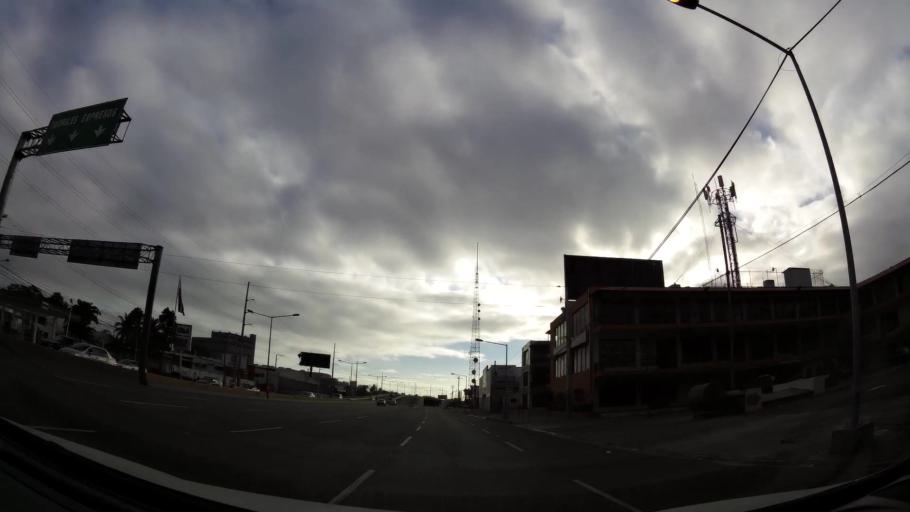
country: DO
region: Nacional
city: Bella Vista
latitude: 18.4808
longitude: -69.9581
